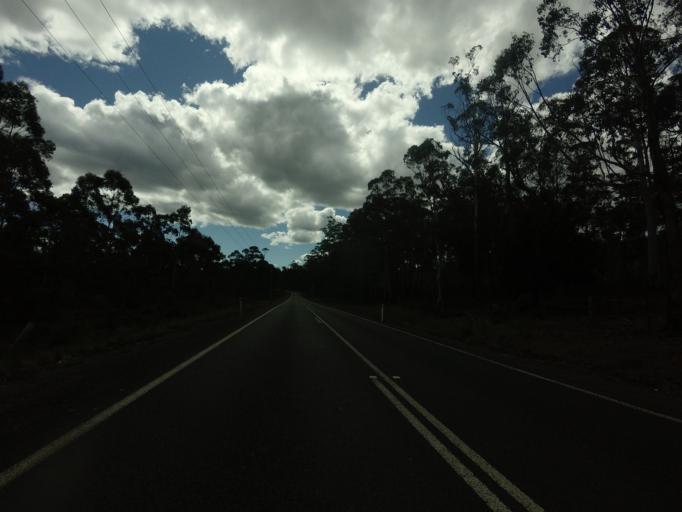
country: AU
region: Tasmania
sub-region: Northern Midlands
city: Evandale
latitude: -41.9911
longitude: 147.7101
